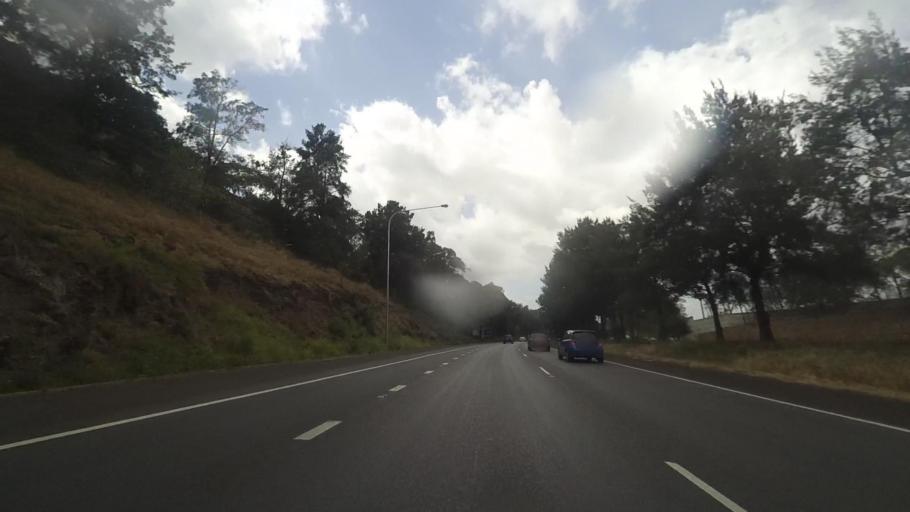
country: AU
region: New South Wales
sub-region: Wollongong
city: Mangerton
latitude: -34.4326
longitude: 150.8684
